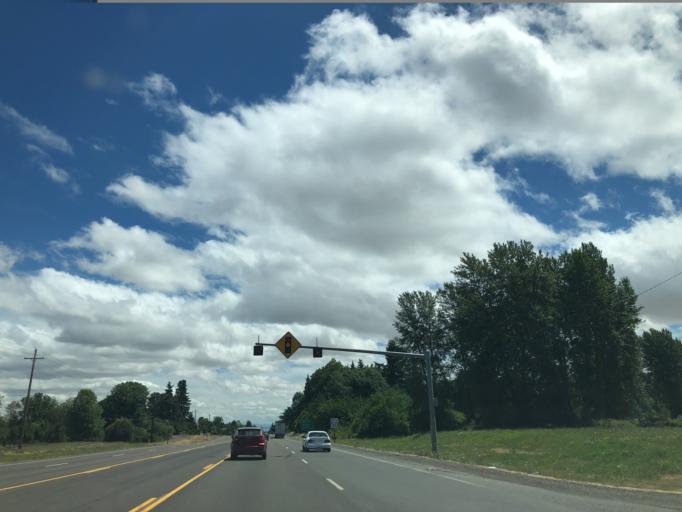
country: US
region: Oregon
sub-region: Benton County
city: Corvallis
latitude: 44.5639
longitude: -123.2417
